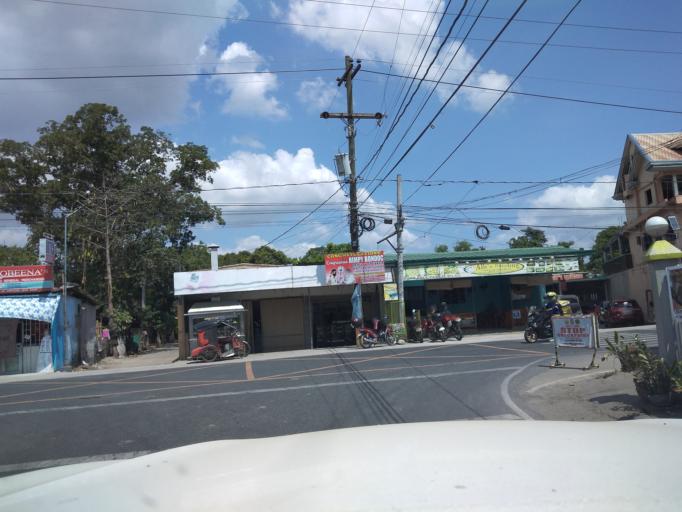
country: PH
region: Central Luzon
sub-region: Province of Pampanga
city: Bahay Pare
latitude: 15.0194
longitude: 120.8868
